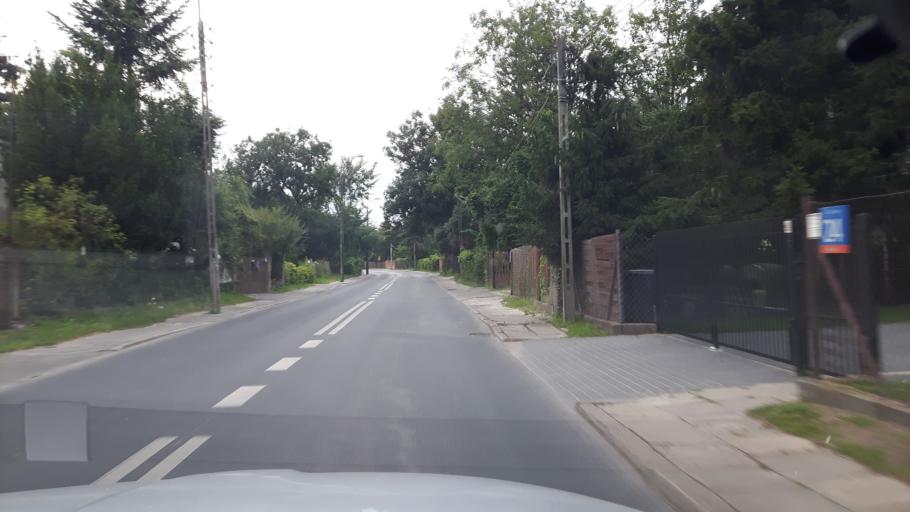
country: PL
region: Masovian Voivodeship
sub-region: Warszawa
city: Praga Poludnie
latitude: 52.2100
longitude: 21.0759
